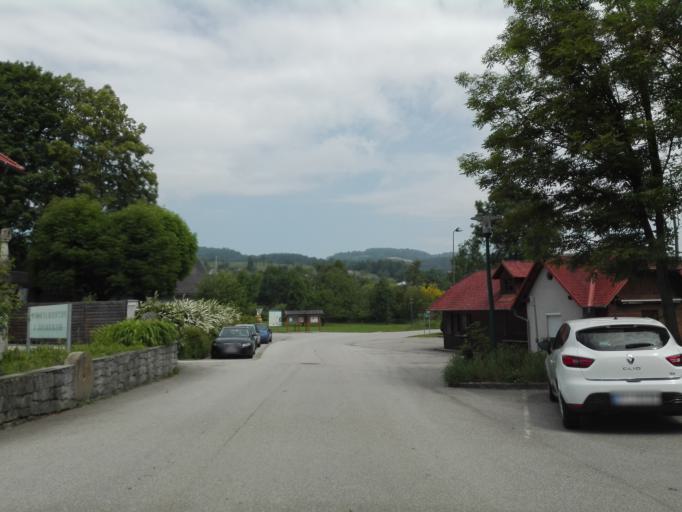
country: AT
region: Upper Austria
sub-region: Politischer Bezirk Urfahr-Umgebung
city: Feldkirchen an der Donau
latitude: 48.3697
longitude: 13.9724
